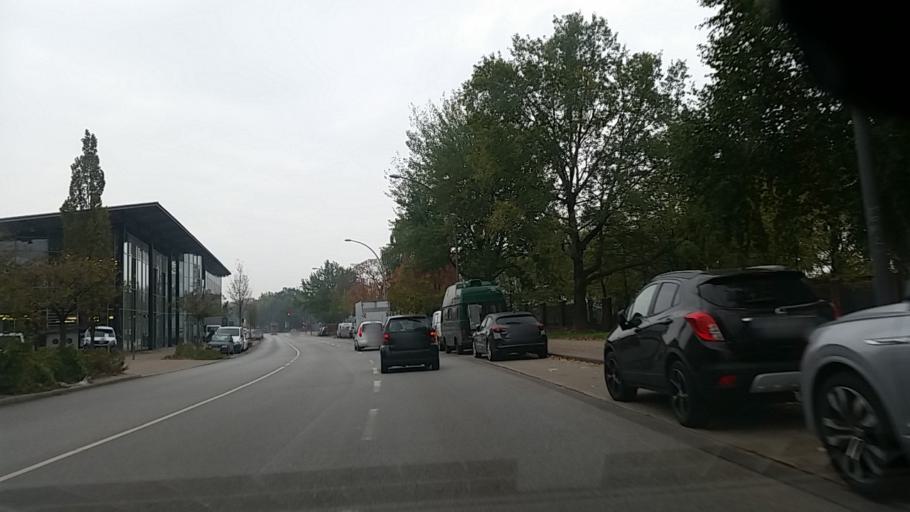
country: DE
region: Hamburg
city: Stellingen
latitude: 53.5699
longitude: 9.9176
